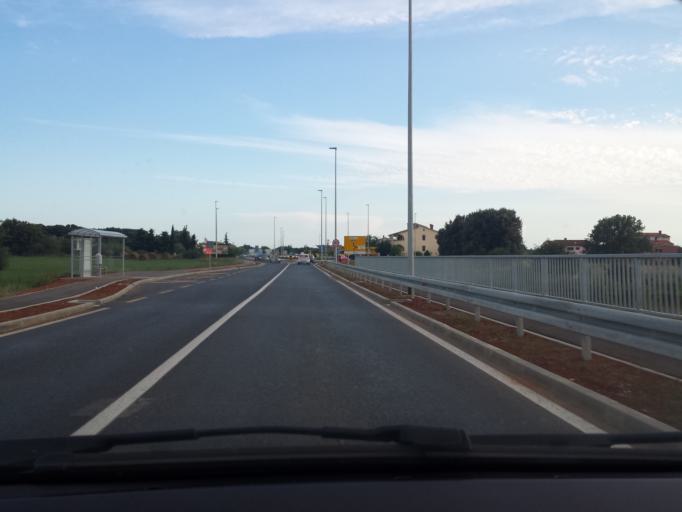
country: HR
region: Istarska
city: Galizana
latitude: 44.9052
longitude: 13.8466
